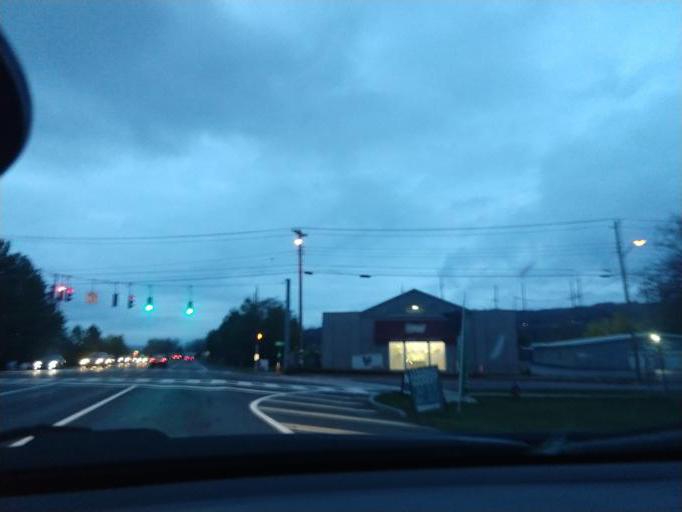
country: US
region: New York
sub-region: Tompkins County
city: Ithaca
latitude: 42.4487
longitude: -76.5065
